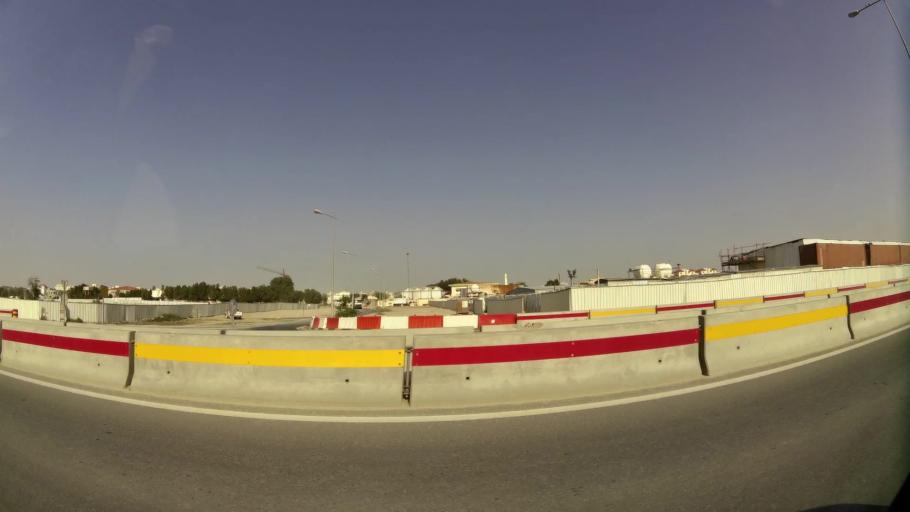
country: QA
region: Baladiyat ar Rayyan
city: Ar Rayyan
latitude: 25.3250
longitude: 51.4480
